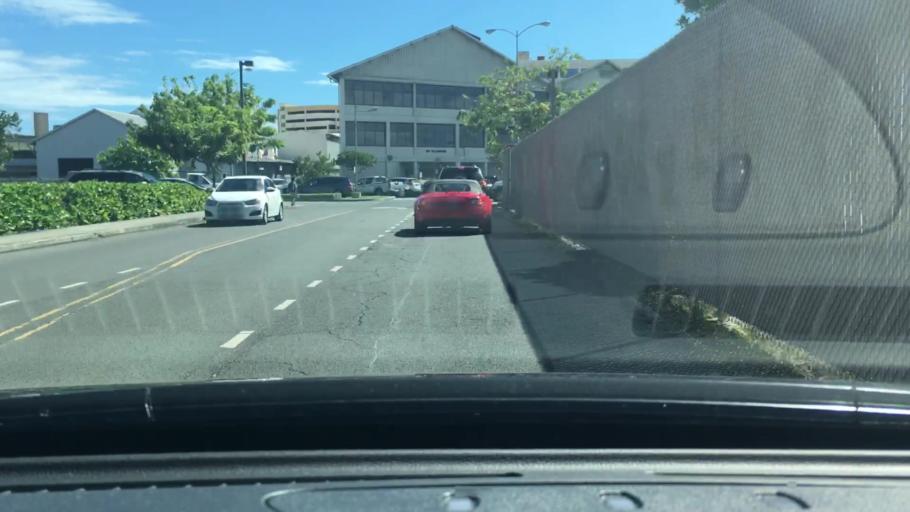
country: US
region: Hawaii
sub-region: Honolulu County
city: Honolulu
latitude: 21.3190
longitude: -157.8687
